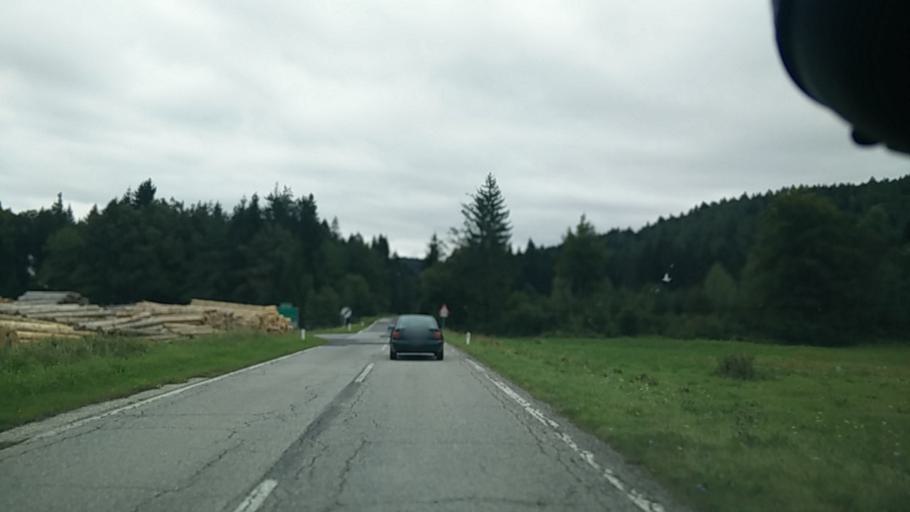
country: AT
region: Carinthia
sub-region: Politischer Bezirk Villach Land
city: Rosegg
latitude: 46.5514
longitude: 13.9953
